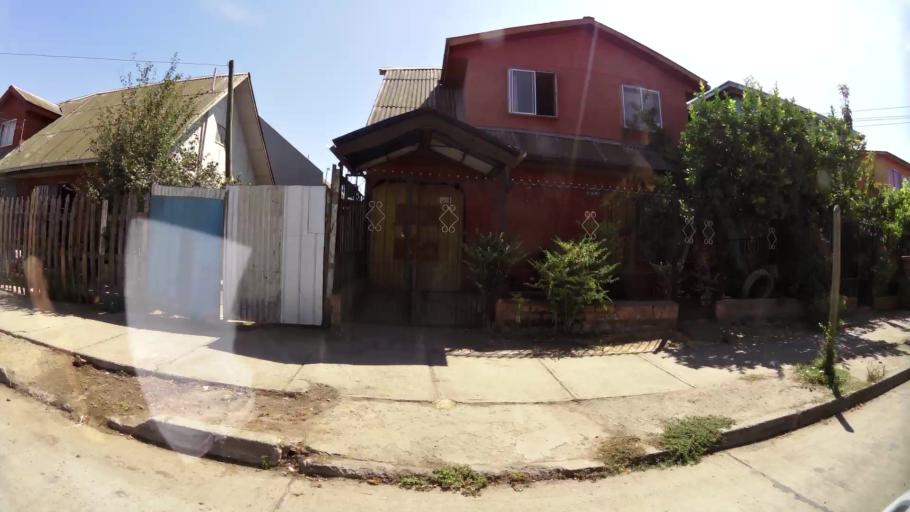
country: CL
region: Maule
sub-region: Provincia de Talca
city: Talca
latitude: -35.4194
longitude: -71.6393
